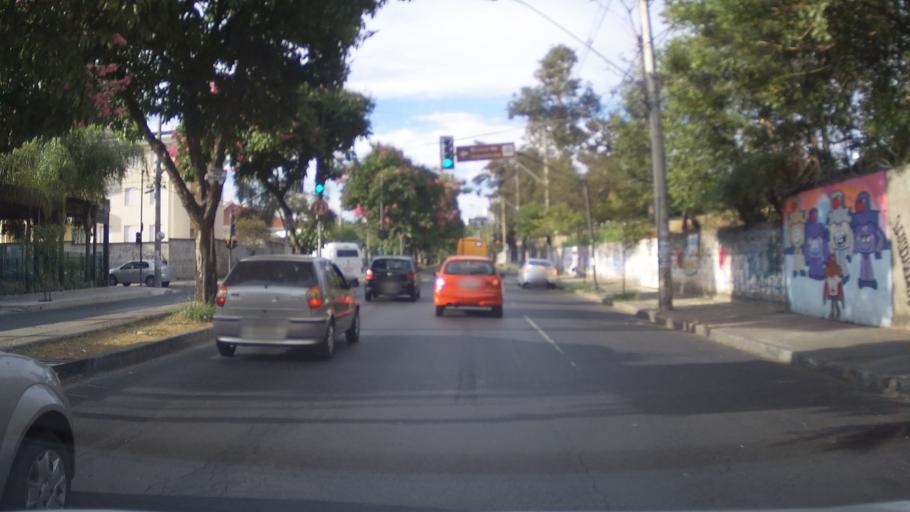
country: BR
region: Minas Gerais
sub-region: Belo Horizonte
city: Belo Horizonte
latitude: -19.8695
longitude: -43.9861
